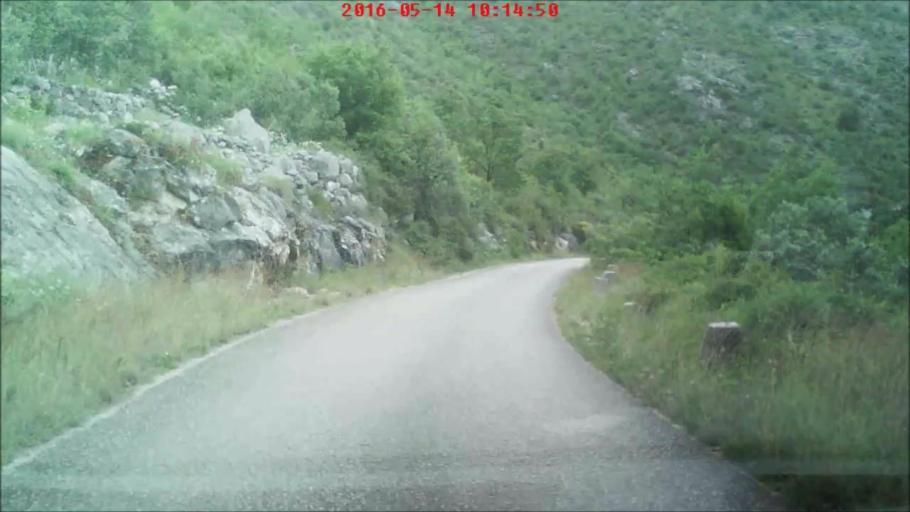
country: HR
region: Dubrovacko-Neretvanska
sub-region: Grad Dubrovnik
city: Mokosica
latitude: 42.7324
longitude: 17.9610
